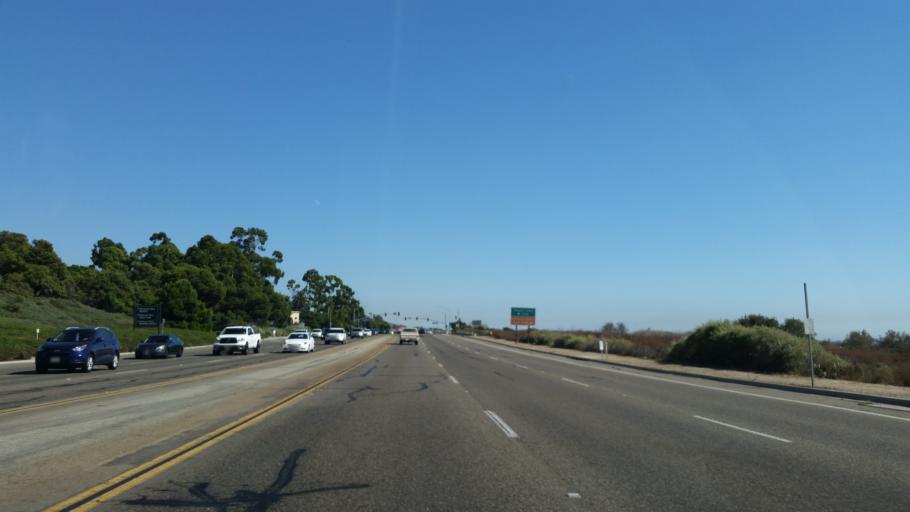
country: US
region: California
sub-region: Orange County
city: San Joaquin Hills
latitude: 33.5847
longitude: -117.8515
